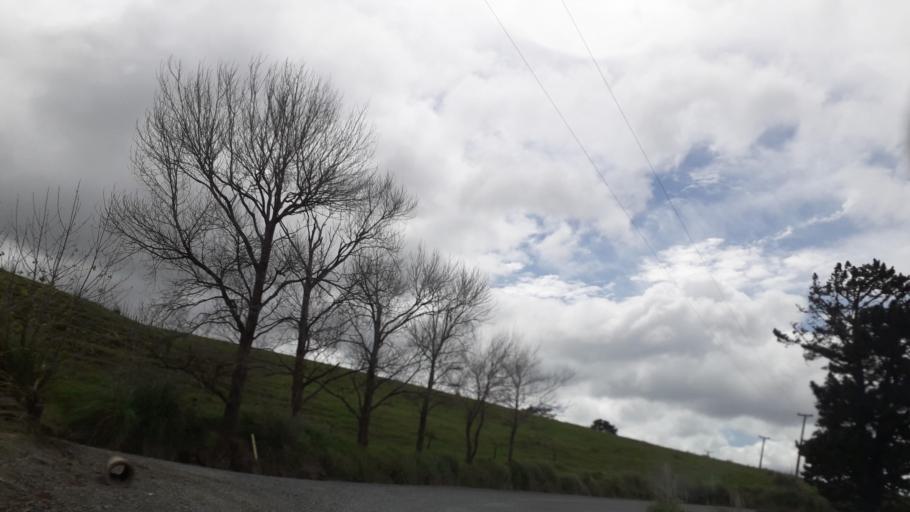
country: NZ
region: Northland
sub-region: Far North District
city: Taipa
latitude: -35.0057
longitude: 173.4313
